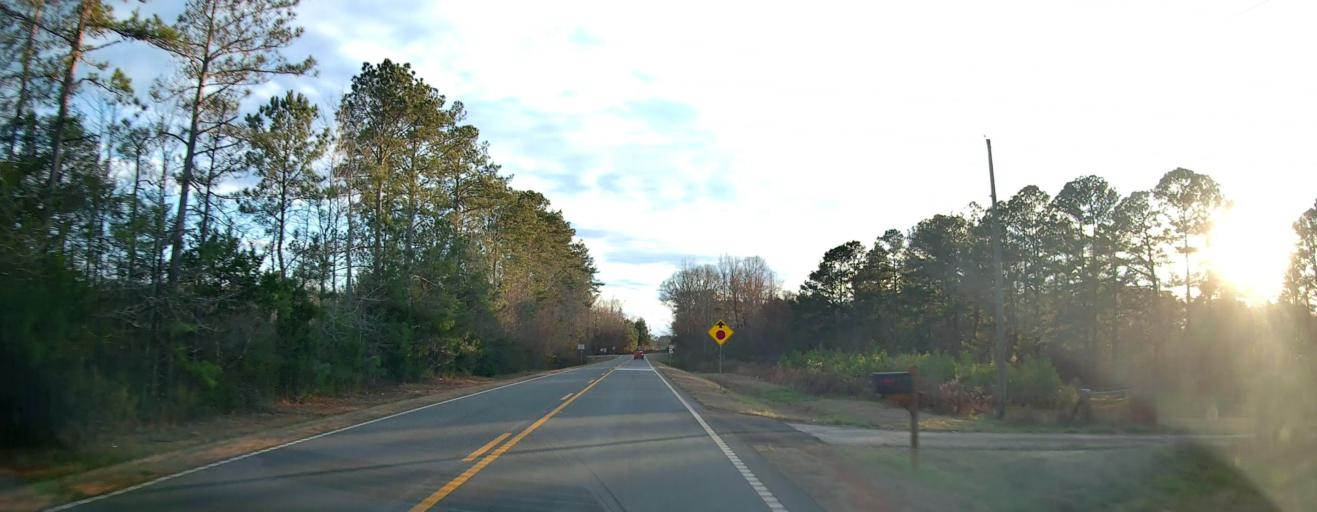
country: US
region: Georgia
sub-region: Talbot County
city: Sardis
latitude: 32.6956
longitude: -84.7022
